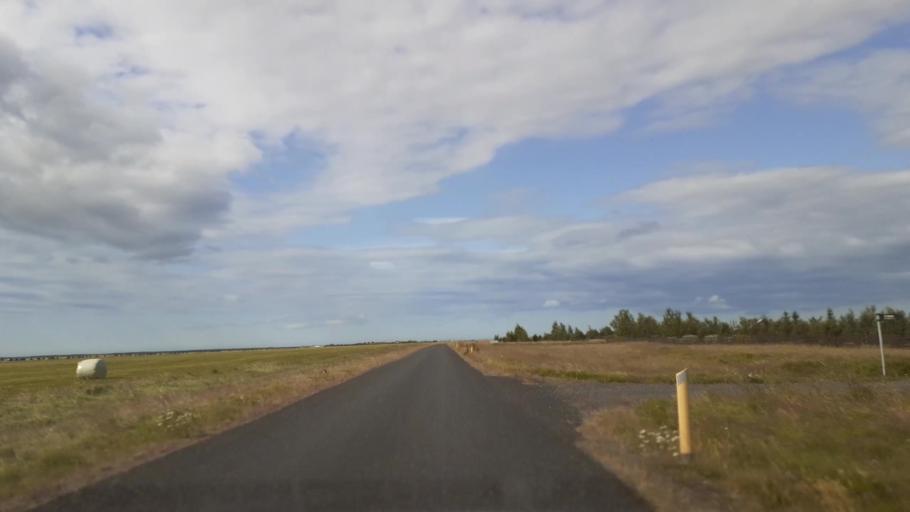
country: IS
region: South
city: Vestmannaeyjar
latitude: 63.7697
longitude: -20.2939
